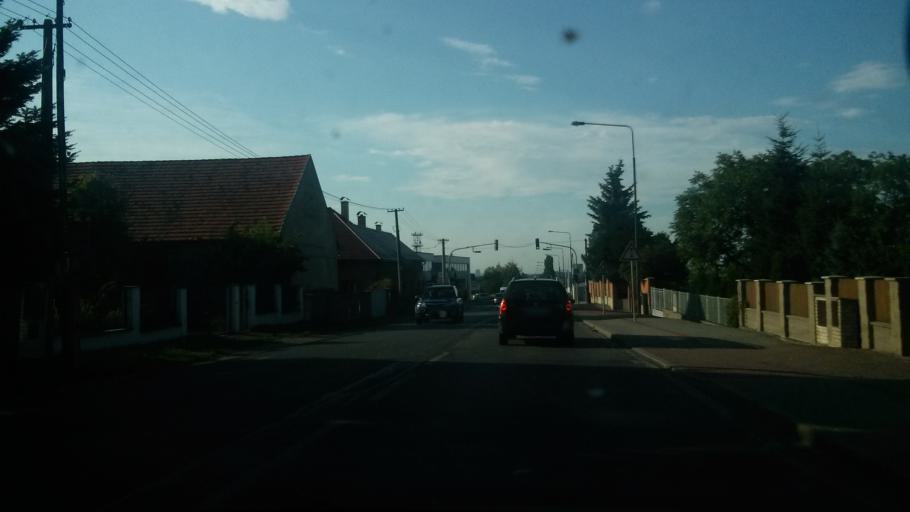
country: CZ
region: Central Bohemia
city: Vestec
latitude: 49.9776
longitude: 14.4997
